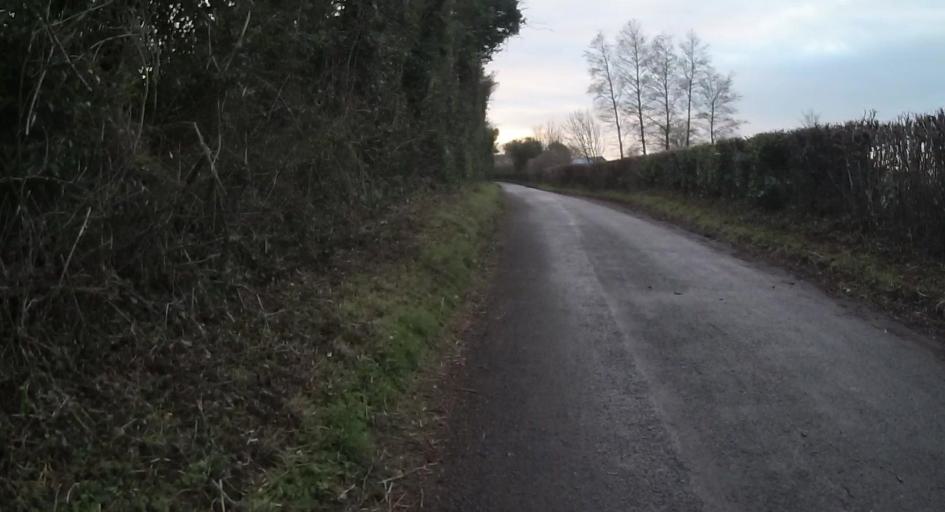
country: GB
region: England
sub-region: Hampshire
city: Swanmore
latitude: 51.0239
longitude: -1.1575
